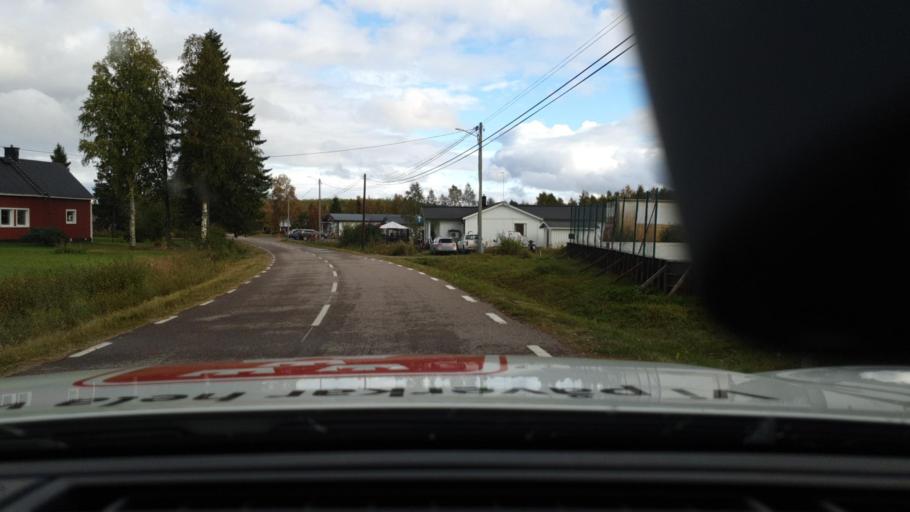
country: SE
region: Norrbotten
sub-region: Overkalix Kommun
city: OEverkalix
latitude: 67.0034
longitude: 22.4939
